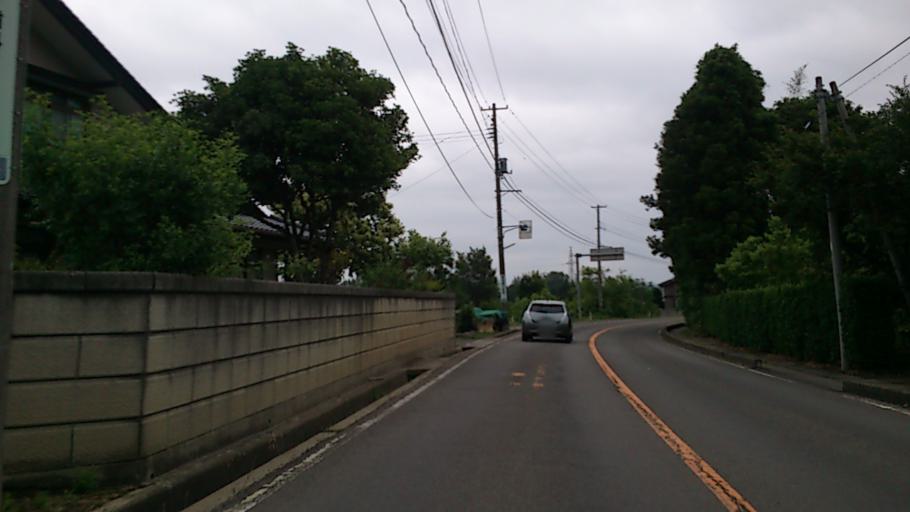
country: JP
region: Fukushima
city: Fukushima-shi
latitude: 37.7587
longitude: 140.4023
